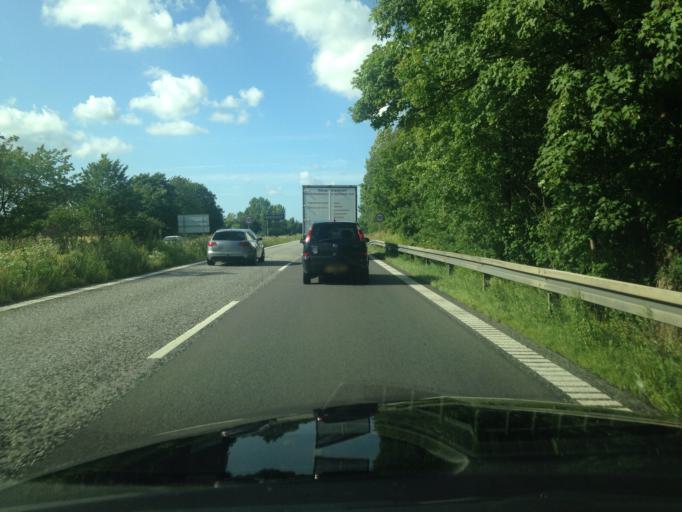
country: DK
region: Capital Region
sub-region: Fredensborg Kommune
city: Kokkedal
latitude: 55.8999
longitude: 12.4743
